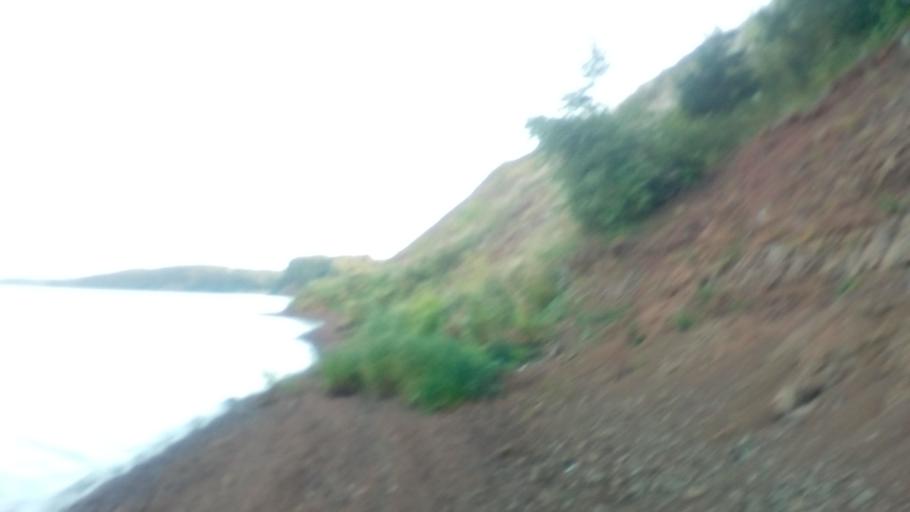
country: RU
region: Perm
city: Usol'ye
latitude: 59.4874
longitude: 56.5870
